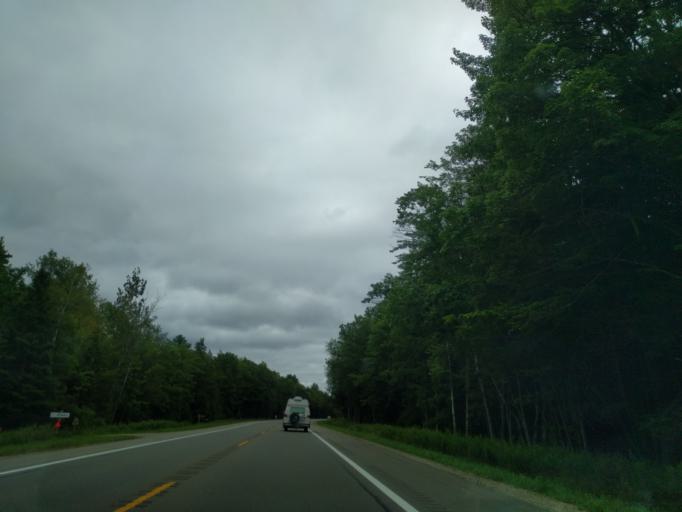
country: US
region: Michigan
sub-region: Menominee County
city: Menominee
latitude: 45.3014
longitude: -87.4395
